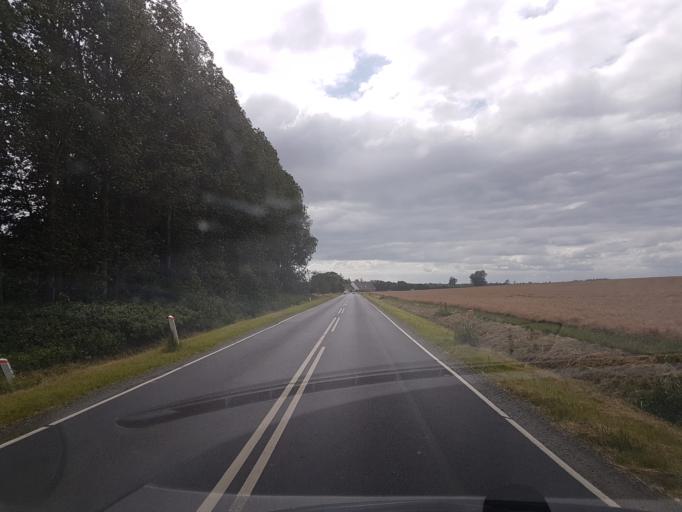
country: DK
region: South Denmark
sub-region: Nordfyns Kommune
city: Bogense
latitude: 55.5700
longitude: 10.1925
